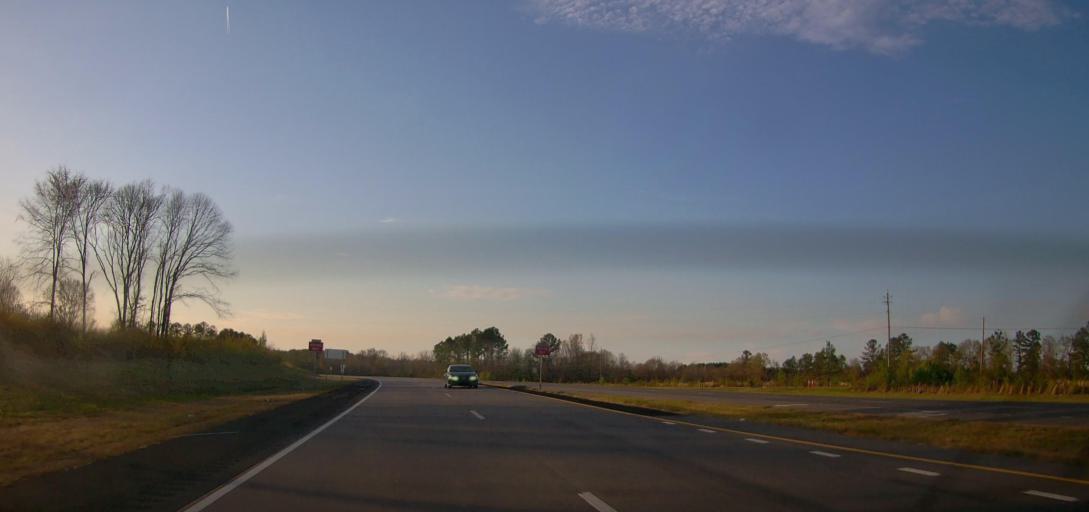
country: US
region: Alabama
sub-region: Talladega County
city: Childersburg
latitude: 33.3008
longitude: -86.3702
